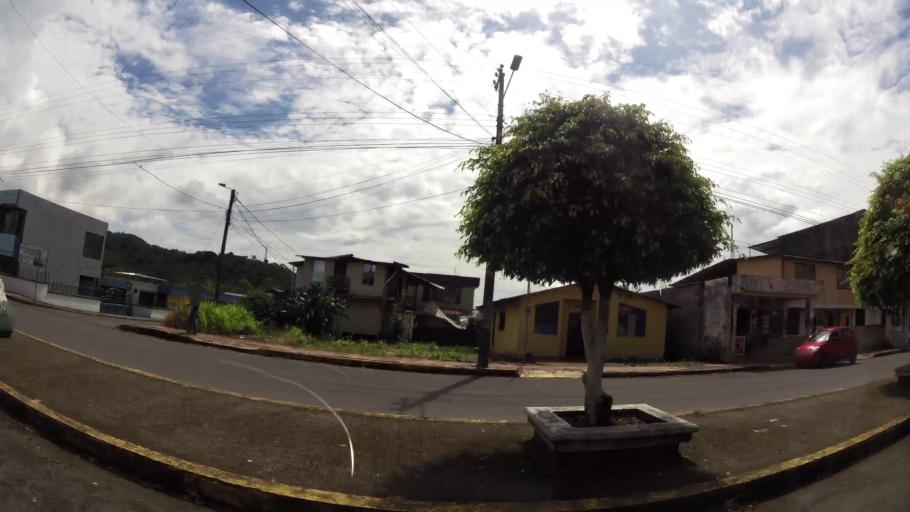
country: EC
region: Pastaza
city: Puyo
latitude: -1.4974
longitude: -78.0610
